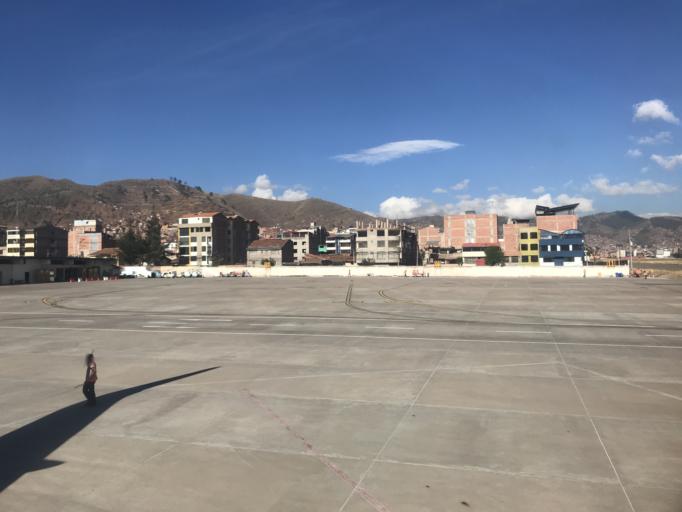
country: PE
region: Cusco
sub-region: Provincia de Cusco
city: Cusco
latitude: -13.5372
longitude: -71.9443
